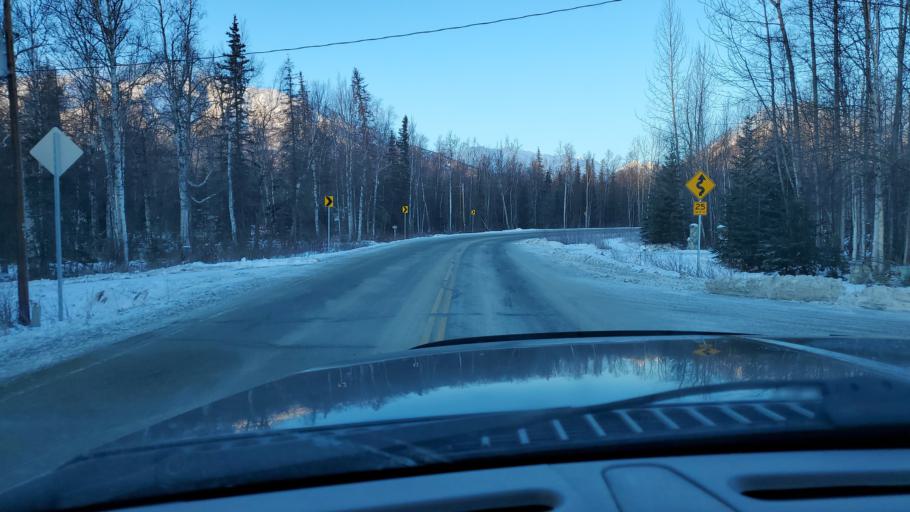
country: US
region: Alaska
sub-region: Matanuska-Susitna Borough
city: Fishhook
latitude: 61.6860
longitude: -149.2464
